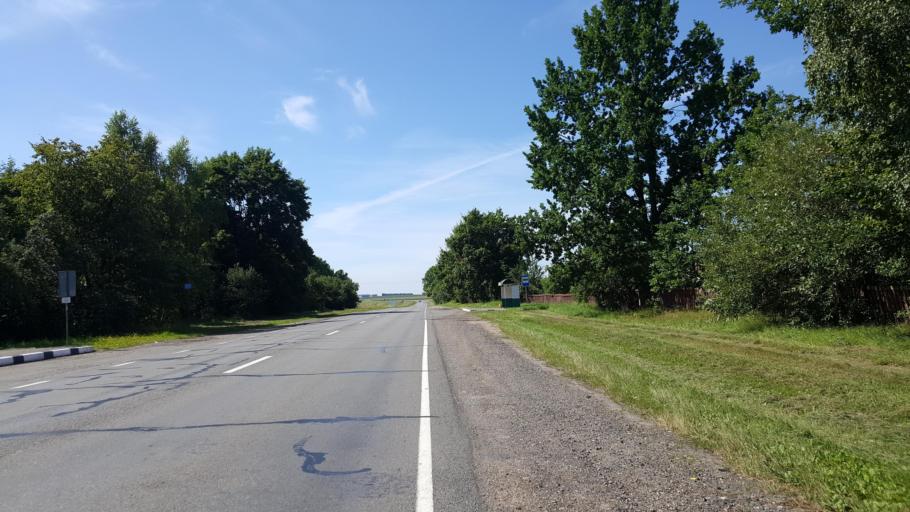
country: BY
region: Brest
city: Charnawchytsy
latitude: 52.2622
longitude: 23.7624
